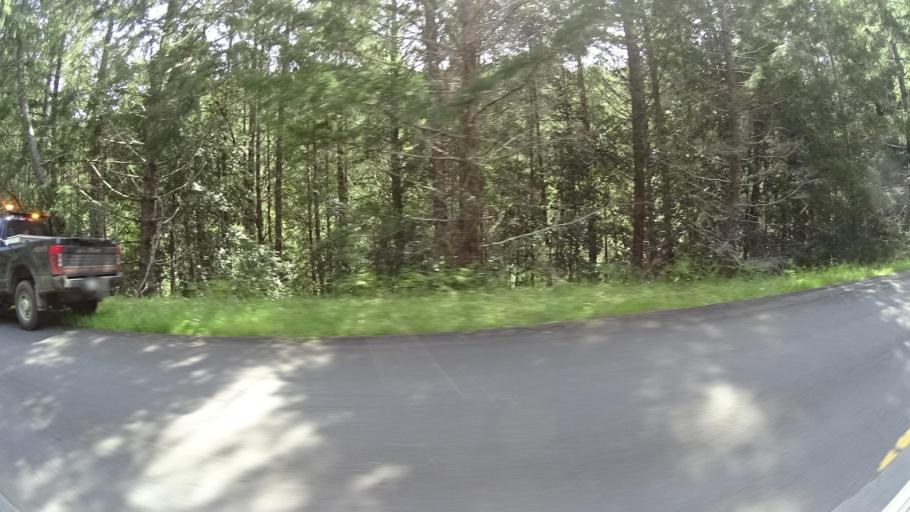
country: US
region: California
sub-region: Humboldt County
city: Redway
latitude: 40.4349
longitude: -123.7751
